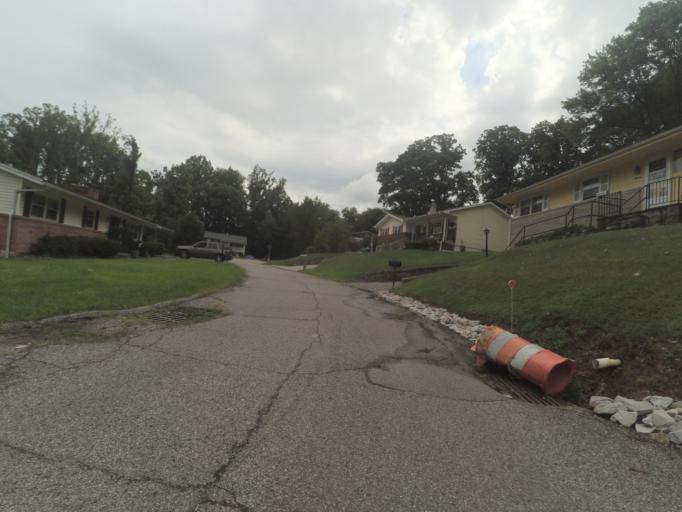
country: US
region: West Virginia
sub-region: Cabell County
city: Huntington
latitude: 38.3984
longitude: -82.4000
